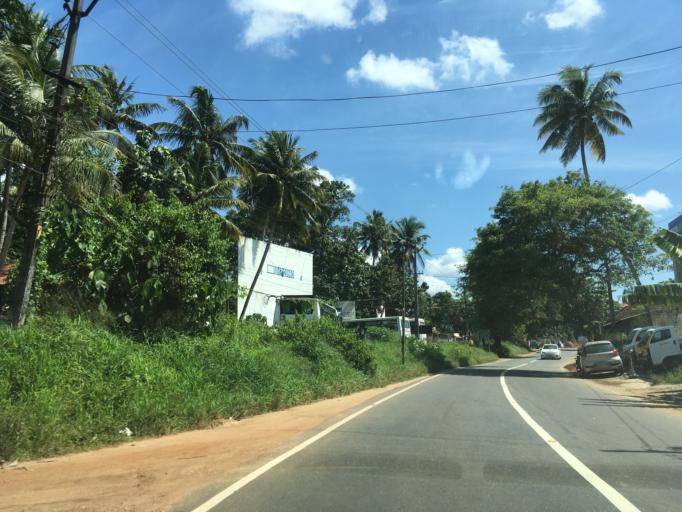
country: IN
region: Kerala
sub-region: Thiruvananthapuram
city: Nedumangad
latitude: 8.5655
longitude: 76.9852
